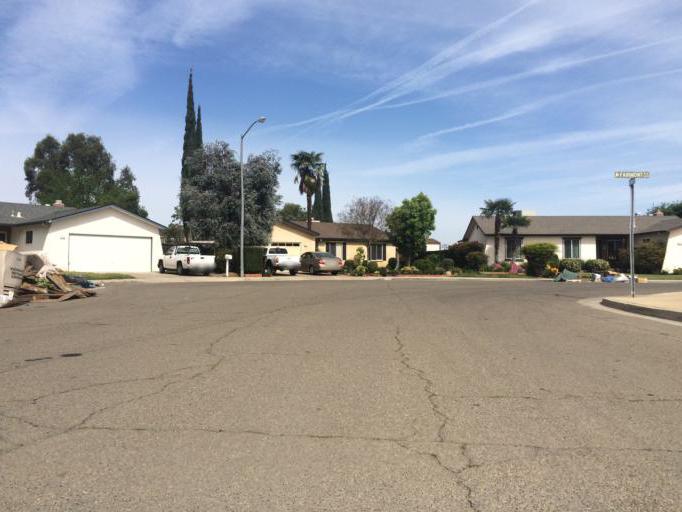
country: US
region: California
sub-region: Fresno County
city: Tarpey Village
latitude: 36.8061
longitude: -119.6846
